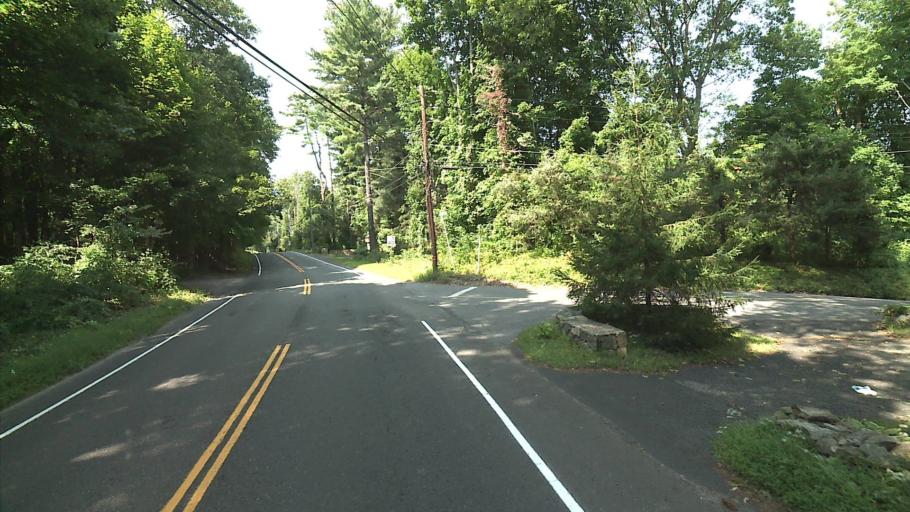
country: US
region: Connecticut
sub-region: Fairfield County
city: Bethel
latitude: 41.3369
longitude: -73.3783
